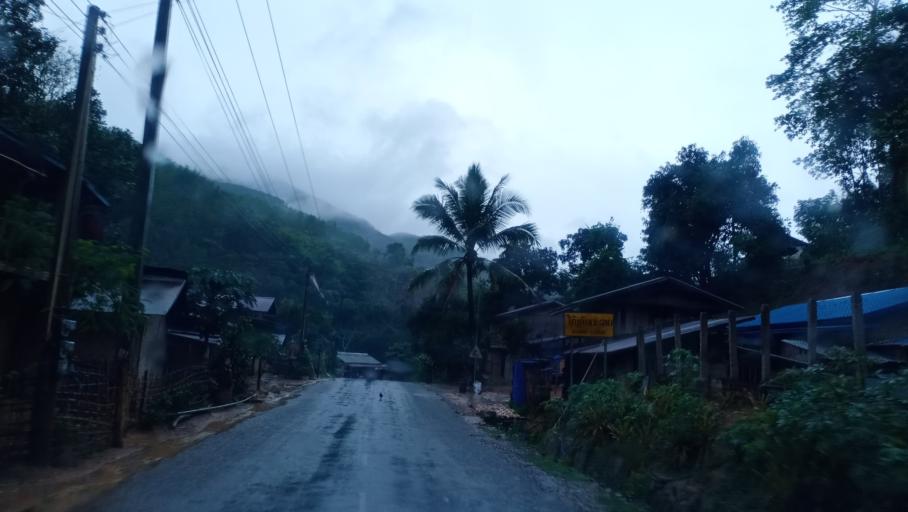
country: LA
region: Phongsali
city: Khoa
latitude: 21.0671
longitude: 102.4894
